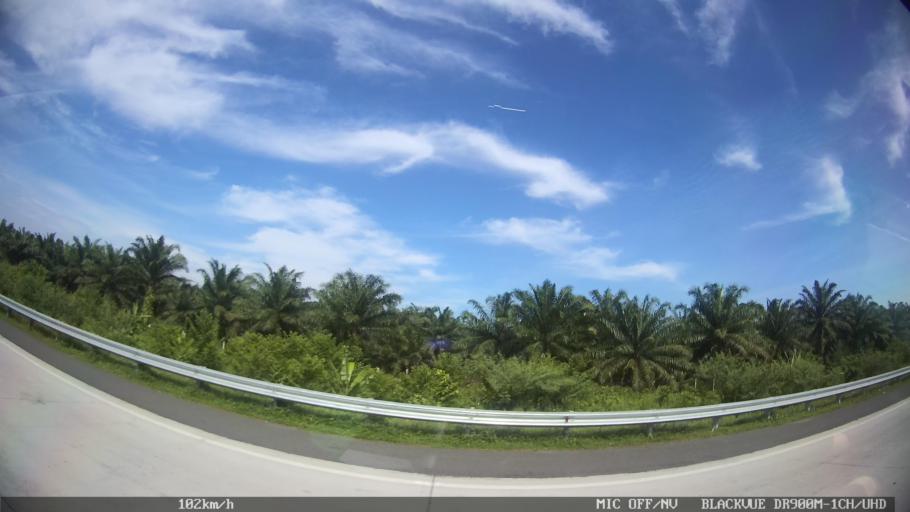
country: ID
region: North Sumatra
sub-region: Kabupaten Langkat
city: Stabat
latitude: 3.6867
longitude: 98.5388
